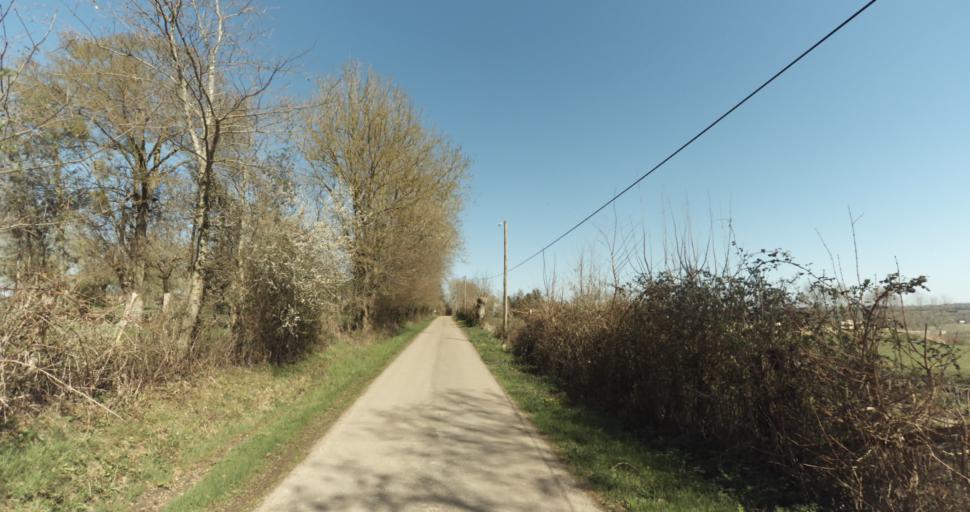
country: FR
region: Lower Normandy
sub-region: Departement du Calvados
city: Saint-Pierre-sur-Dives
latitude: 48.9925
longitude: 0.0564
